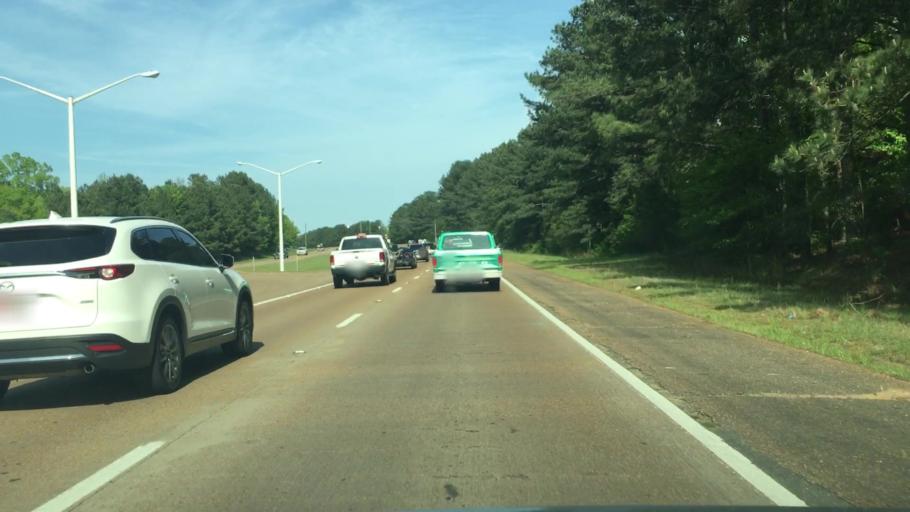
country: US
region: Mississippi
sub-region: Rankin County
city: Brandon
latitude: 32.3610
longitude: -89.9979
